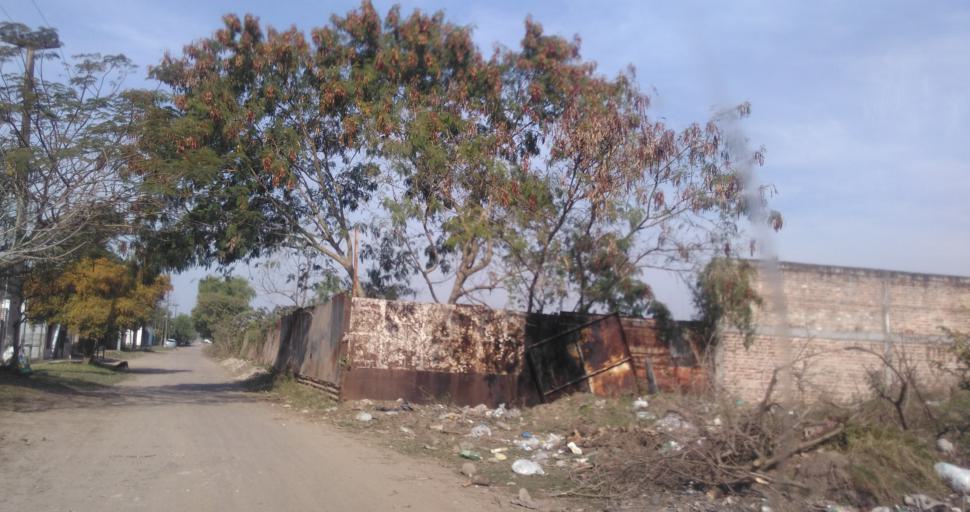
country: AR
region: Chaco
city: Fontana
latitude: -27.4315
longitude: -59.0195
